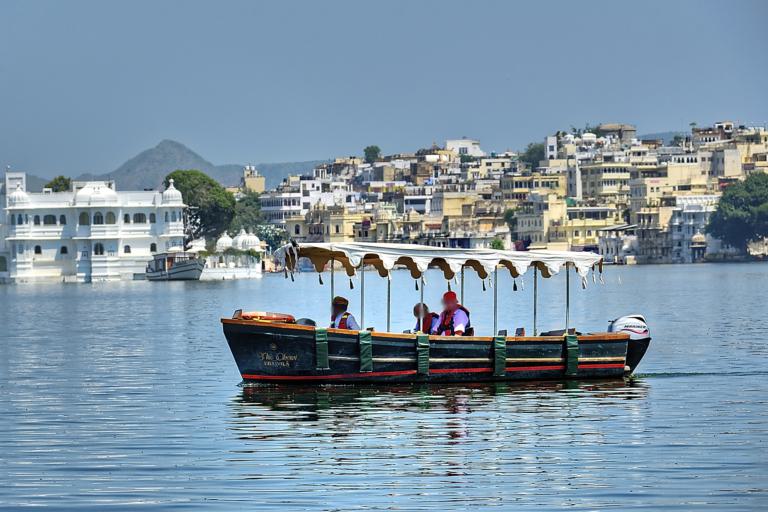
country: IN
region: Rajasthan
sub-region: Udaipur
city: Udaipur
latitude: 24.5678
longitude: 73.6784
